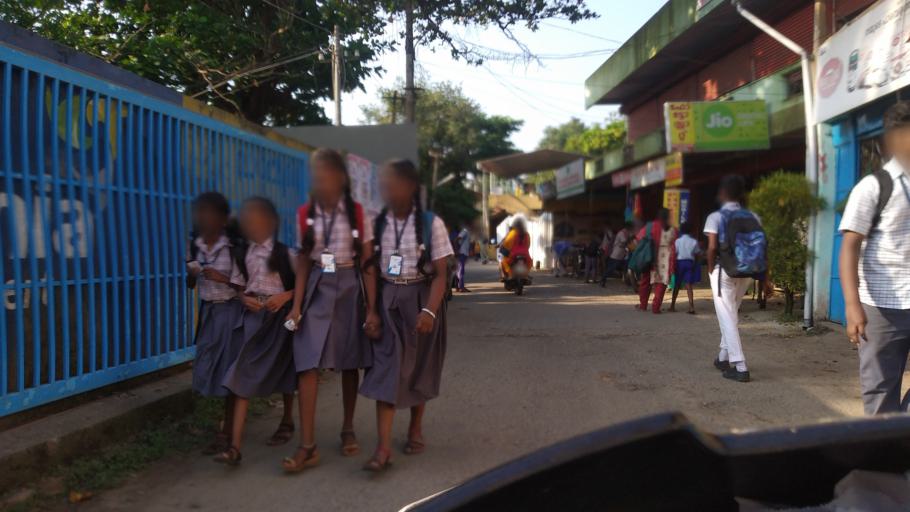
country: IN
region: Kerala
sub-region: Ernakulam
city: Elur
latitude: 10.0489
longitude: 76.2195
